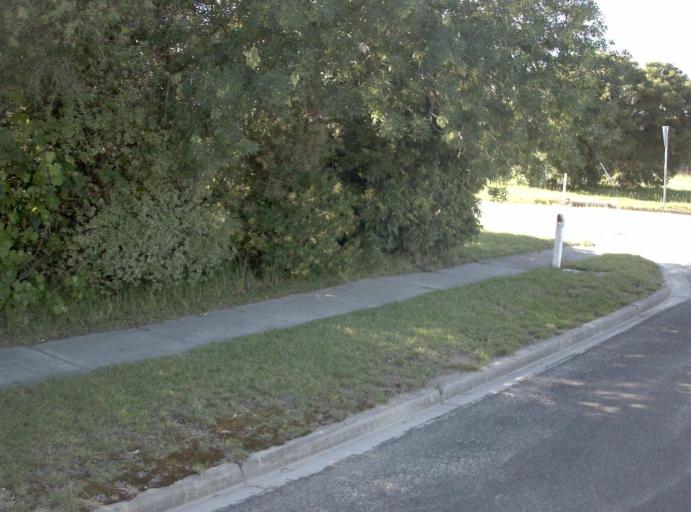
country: AU
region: Victoria
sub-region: East Gippsland
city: Lakes Entrance
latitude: -37.6935
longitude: 148.4581
